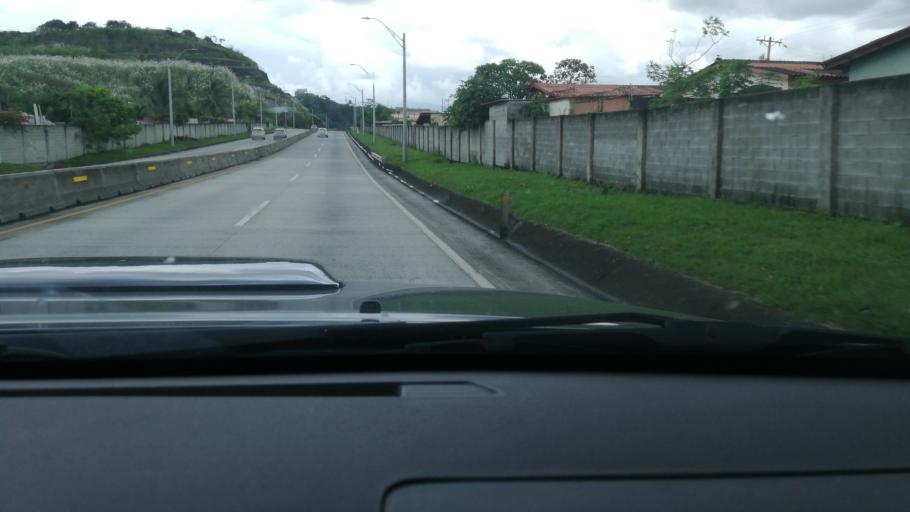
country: PA
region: Panama
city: San Miguelito
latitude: 9.0552
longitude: -79.4828
